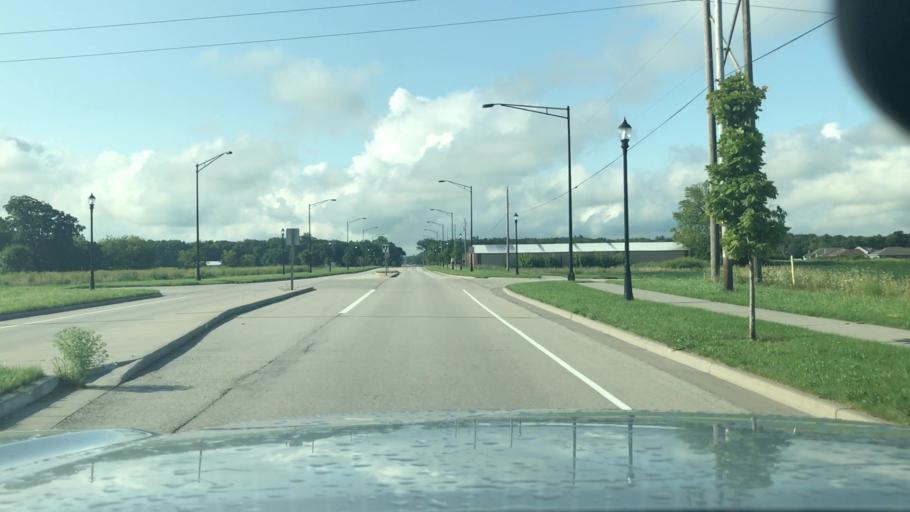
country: US
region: Wisconsin
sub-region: Brown County
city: Bellevue
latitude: 44.4644
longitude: -87.9174
